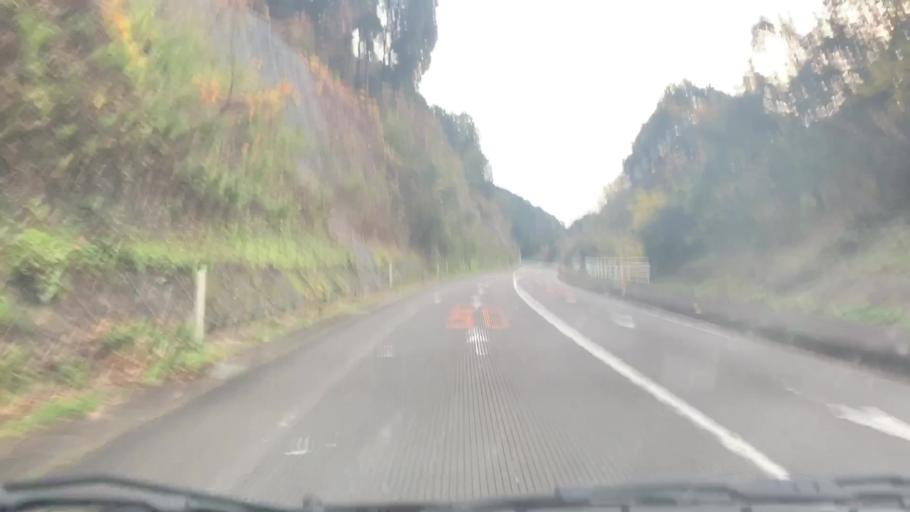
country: JP
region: Saga Prefecture
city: Kashima
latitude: 33.0461
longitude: 130.0717
